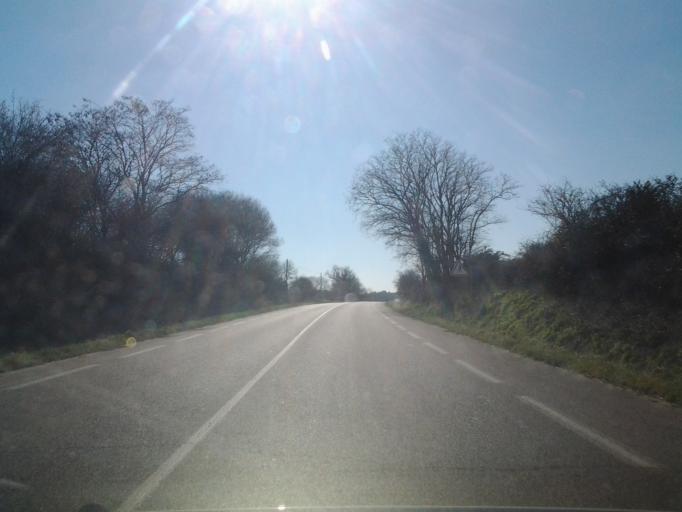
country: FR
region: Pays de la Loire
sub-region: Departement de la Vendee
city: Olonne-sur-Mer
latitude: 46.5418
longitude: -1.7405
